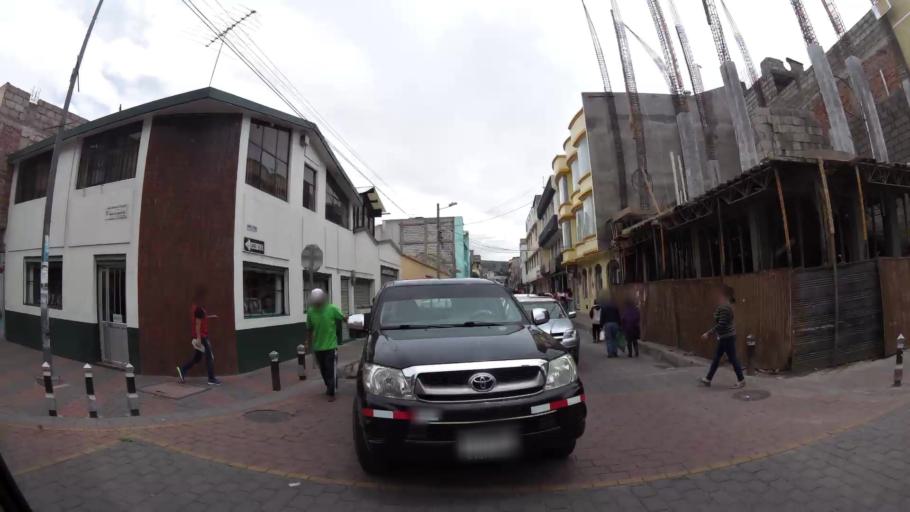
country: EC
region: Cotopaxi
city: San Miguel de Salcedo
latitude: -1.0447
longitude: -78.5903
